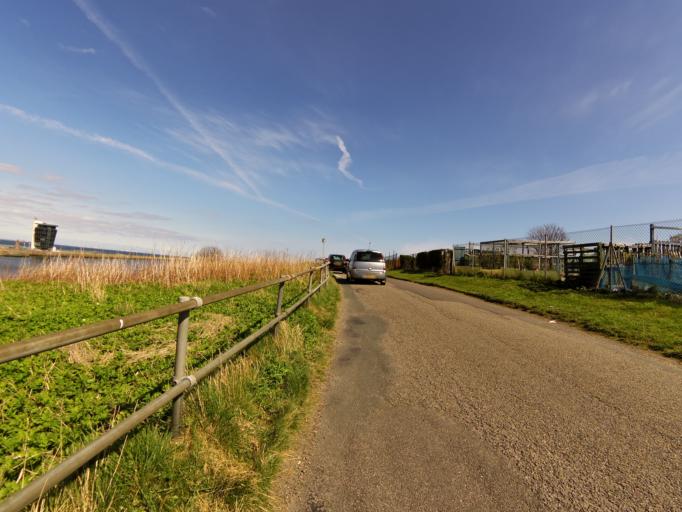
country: GB
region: Scotland
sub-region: Aberdeen City
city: Aberdeen
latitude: 57.1397
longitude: -2.0707
